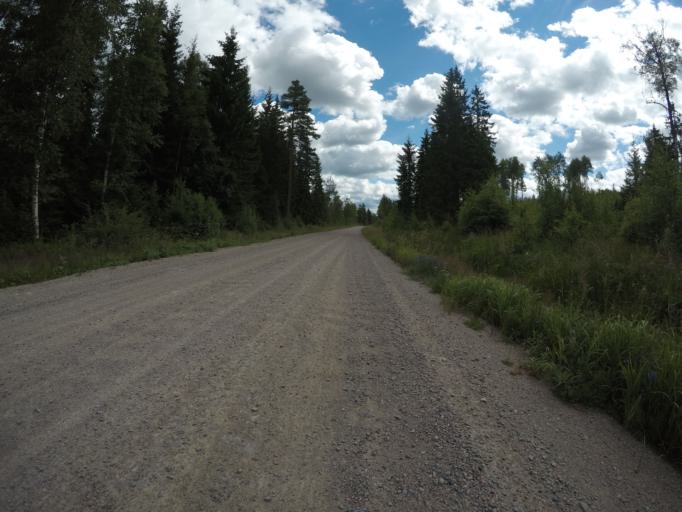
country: SE
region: Vaermland
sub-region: Filipstads Kommun
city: Lesjofors
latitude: 60.1309
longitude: 14.4184
